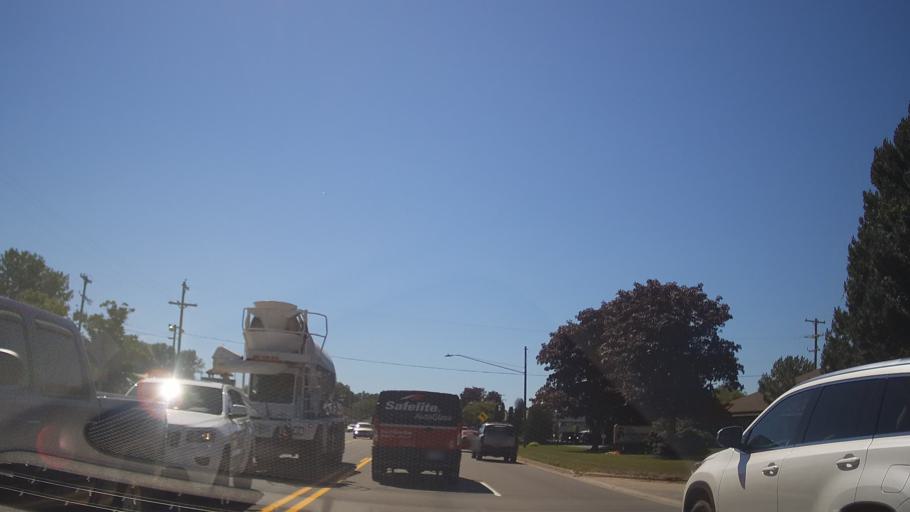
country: US
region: Michigan
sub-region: Emmet County
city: Petoskey
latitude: 45.3893
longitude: -84.9136
